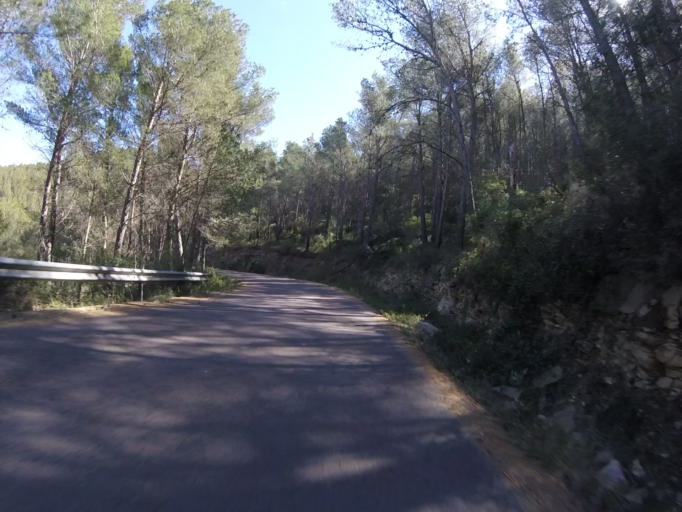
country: ES
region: Valencia
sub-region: Provincia de Castello
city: Cervera del Maestre
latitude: 40.4094
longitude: 0.1956
